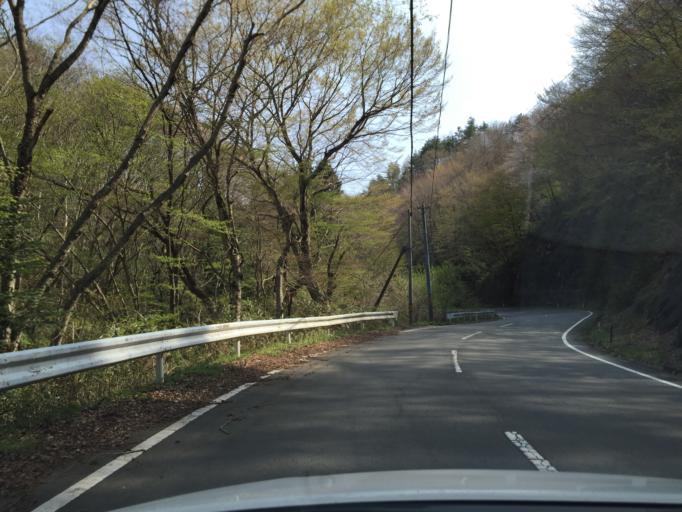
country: JP
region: Fukushima
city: Iwaki
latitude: 37.2380
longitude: 140.8462
